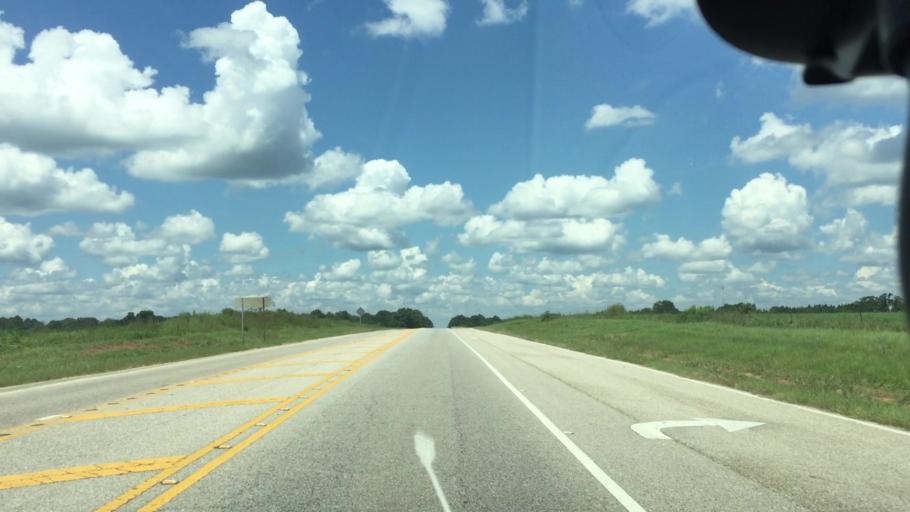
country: US
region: Alabama
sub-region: Coffee County
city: New Brockton
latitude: 31.4169
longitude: -85.8854
